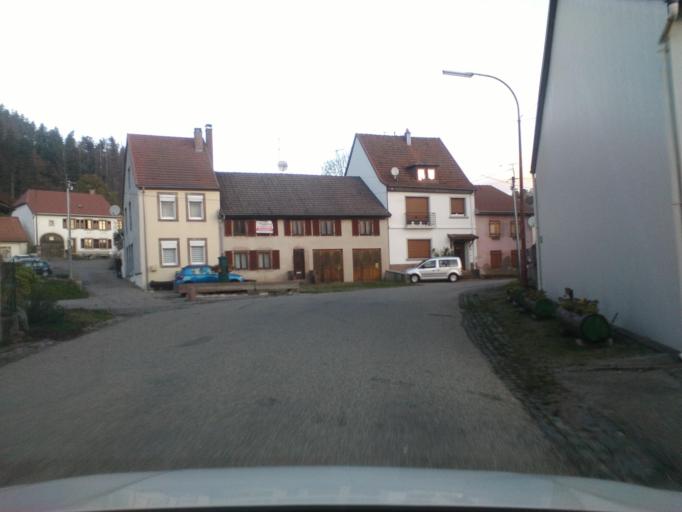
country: FR
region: Lorraine
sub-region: Departement des Vosges
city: Ban-de-Laveline
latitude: 48.3500
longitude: 7.1063
